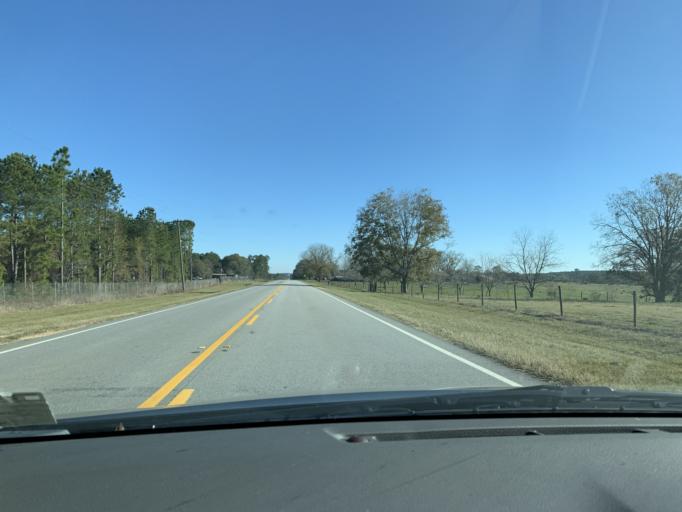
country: US
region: Georgia
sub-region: Ben Hill County
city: Fitzgerald
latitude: 31.7417
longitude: -83.1532
